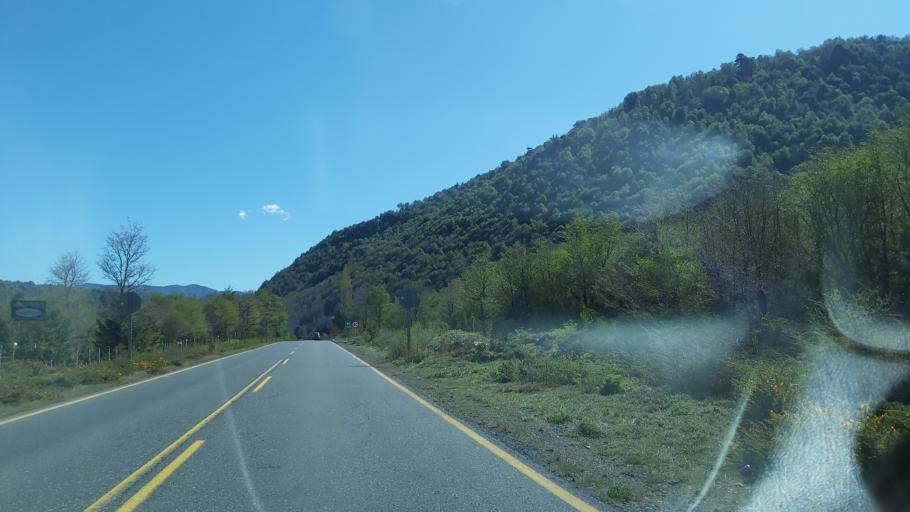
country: CL
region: Araucania
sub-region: Provincia de Cautin
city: Vilcun
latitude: -38.4624
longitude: -71.6324
